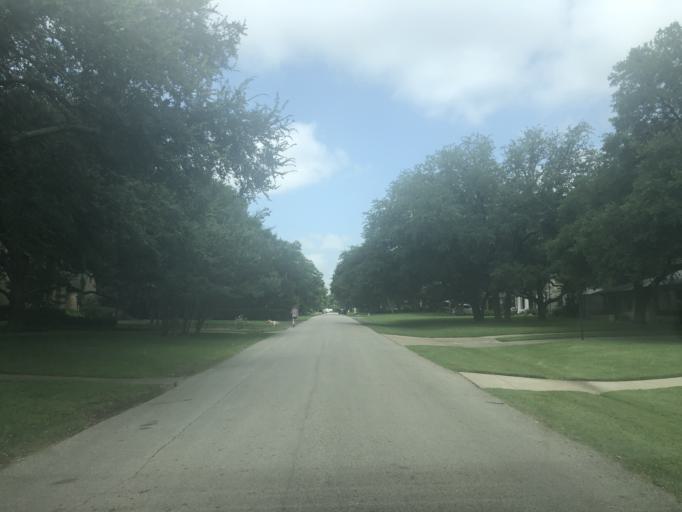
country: US
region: Texas
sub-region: Dallas County
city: University Park
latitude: 32.8687
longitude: -96.8303
